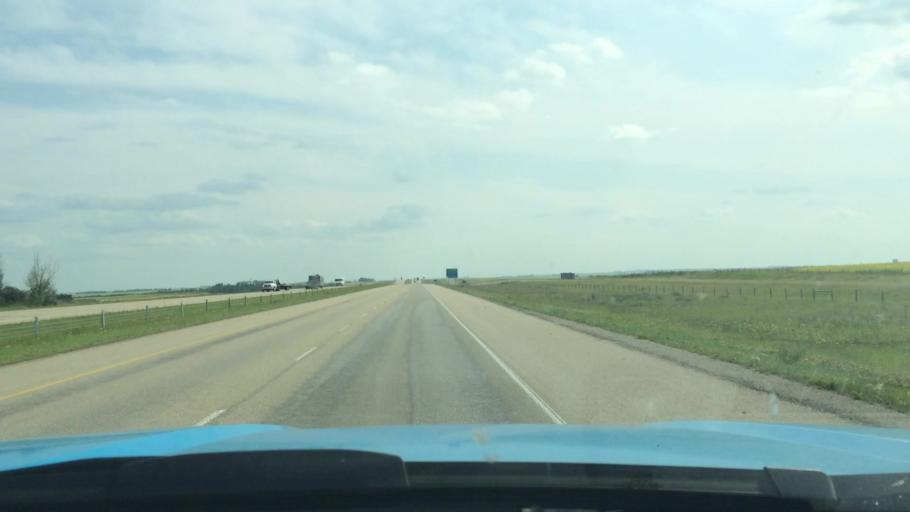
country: CA
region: Alberta
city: Carstairs
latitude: 51.5854
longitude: -114.0253
